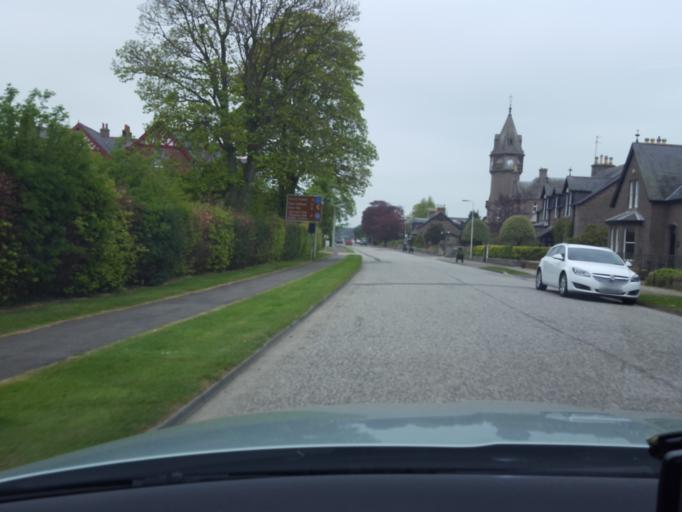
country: GB
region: Scotland
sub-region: Angus
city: Brechin
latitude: 56.8061
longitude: -2.6536
